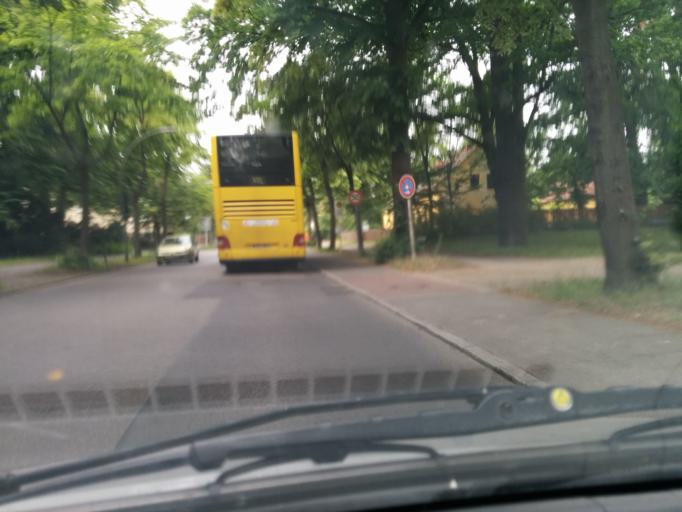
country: DE
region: Berlin
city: Zehlendorf Bezirk
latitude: 52.4369
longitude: 13.2530
